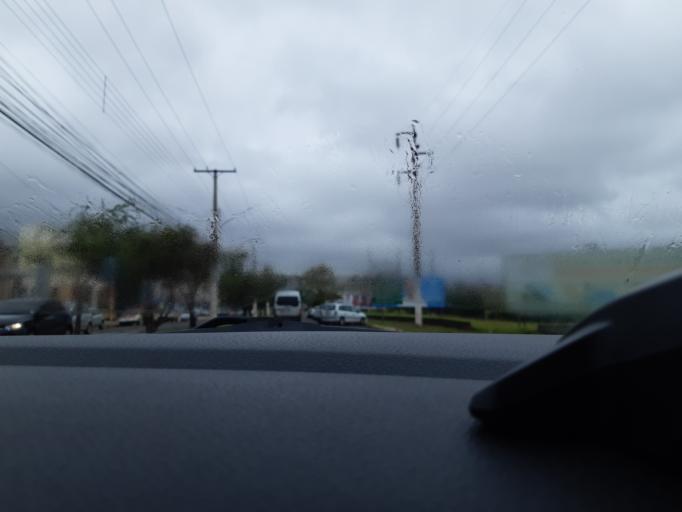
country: BR
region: Sao Paulo
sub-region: Ourinhos
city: Ourinhos
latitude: -22.9752
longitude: -49.8952
